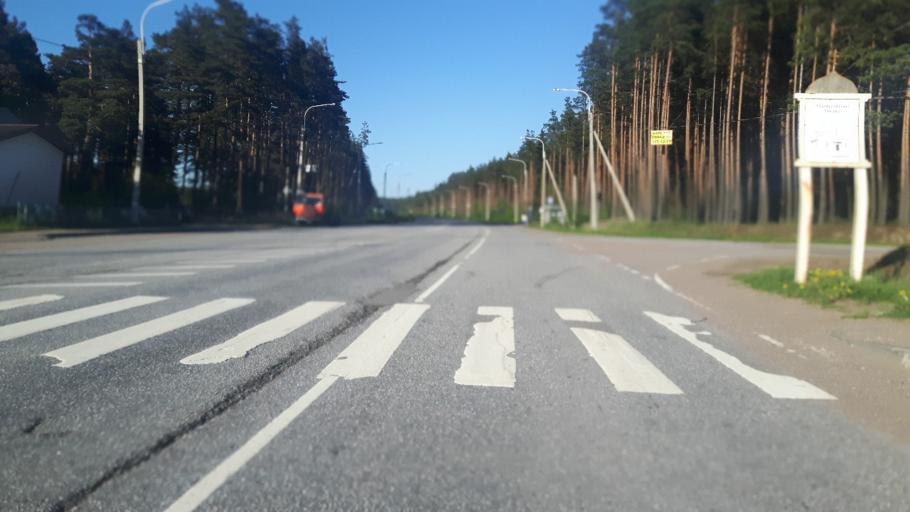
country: RU
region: Leningrad
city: Molodezhnoye
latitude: 60.1696
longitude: 29.4267
